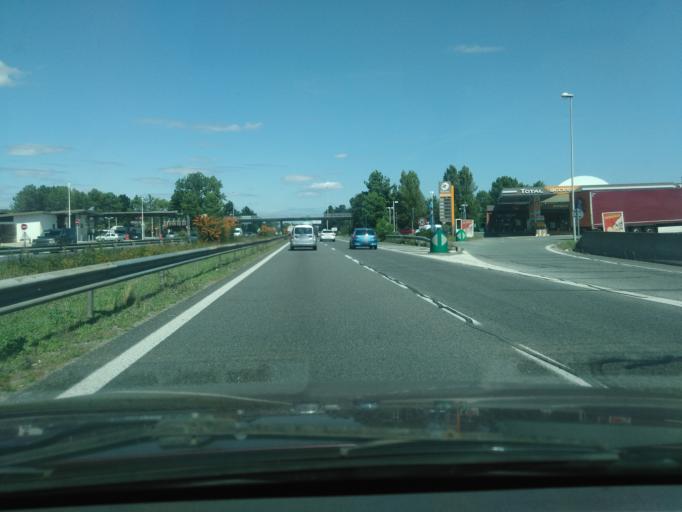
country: FR
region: Aquitaine
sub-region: Departement de la Gironde
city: Le Haillan
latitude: 44.8497
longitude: -0.6679
